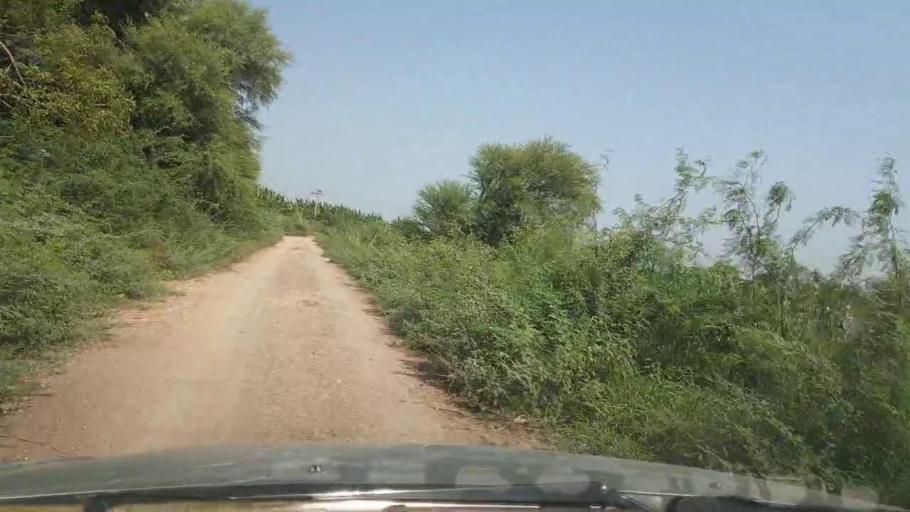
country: PK
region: Sindh
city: Tando Ghulam Ali
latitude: 25.1452
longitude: 68.8853
